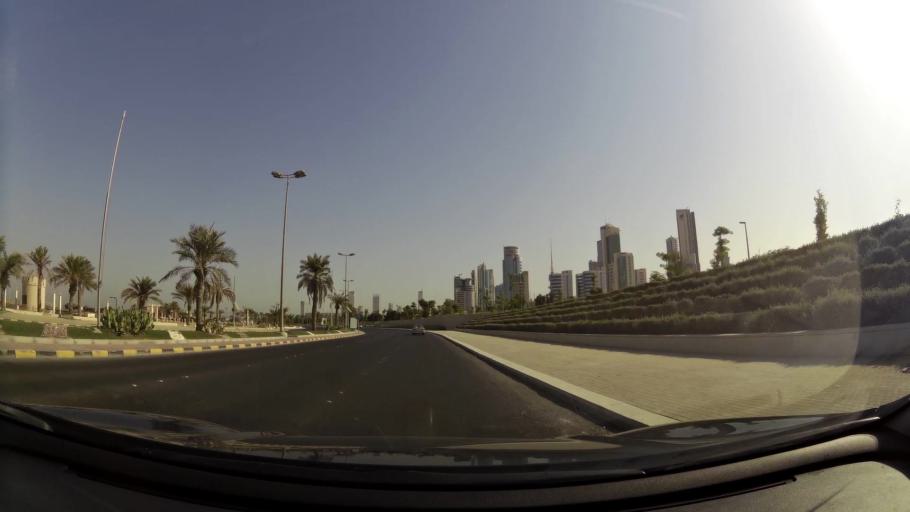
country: KW
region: Al Asimah
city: Ash Shamiyah
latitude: 29.3612
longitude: 47.9561
